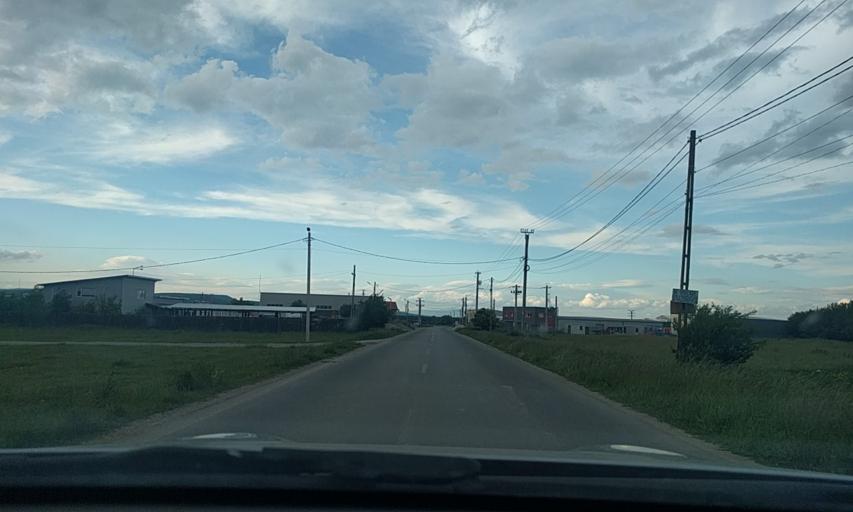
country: RO
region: Brasov
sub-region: Comuna Harman
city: Harman
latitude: 45.7232
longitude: 25.6970
